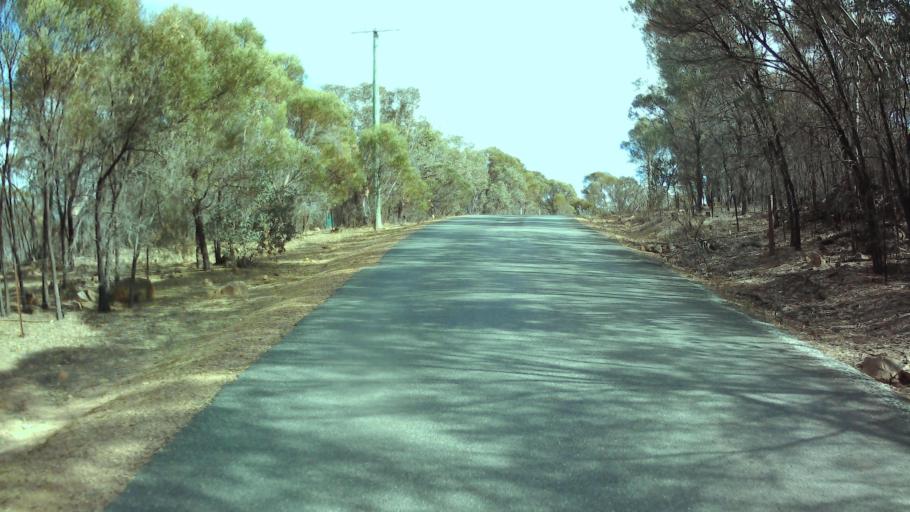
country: AU
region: New South Wales
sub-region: Weddin
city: Grenfell
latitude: -33.8783
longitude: 148.1926
